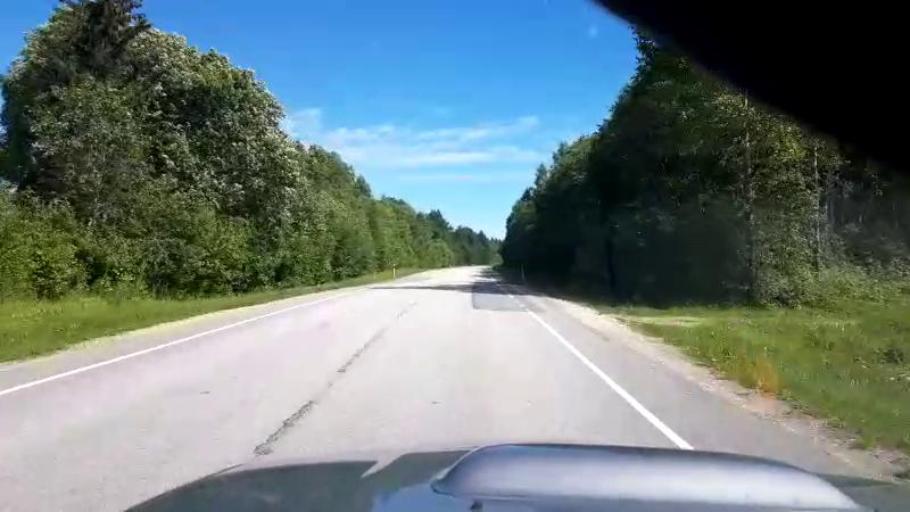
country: EE
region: Jaervamaa
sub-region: Koeru vald
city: Koeru
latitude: 58.9762
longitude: 26.1096
